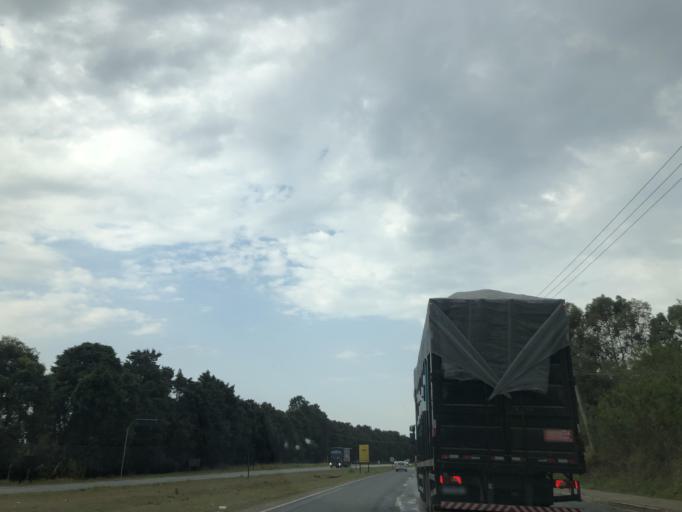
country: BR
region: Sao Paulo
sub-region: Salto De Pirapora
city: Salto de Pirapora
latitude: -23.5807
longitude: -47.5271
